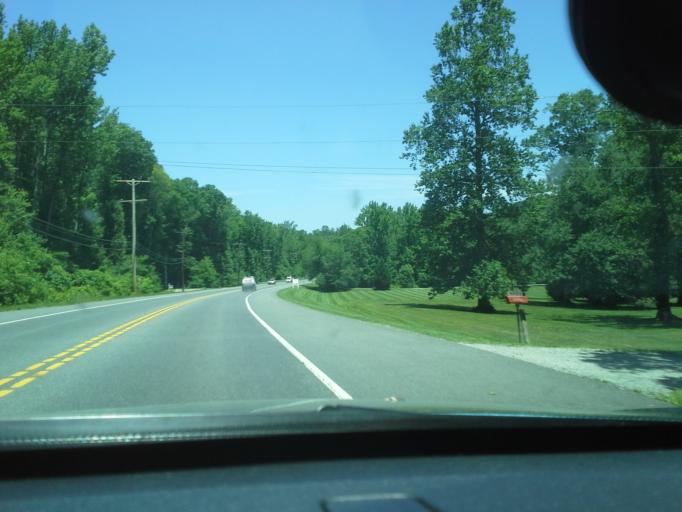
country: US
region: Maryland
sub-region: Anne Arundel County
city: Shady Side
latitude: 38.8618
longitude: -76.5612
